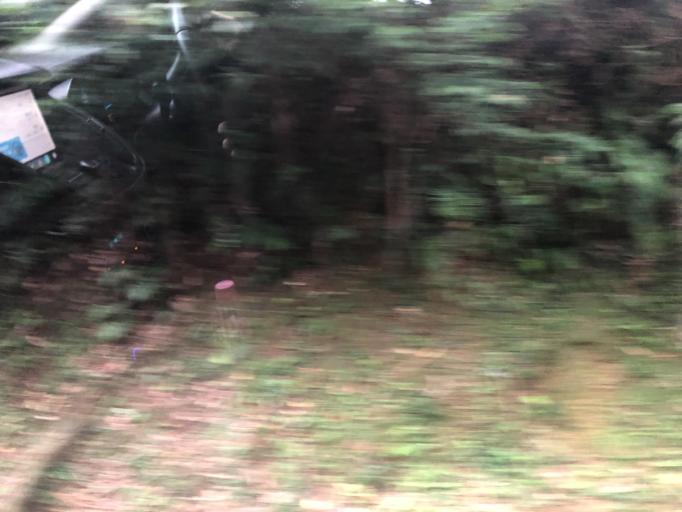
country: TW
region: Taiwan
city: Daxi
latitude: 24.8872
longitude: 121.4214
